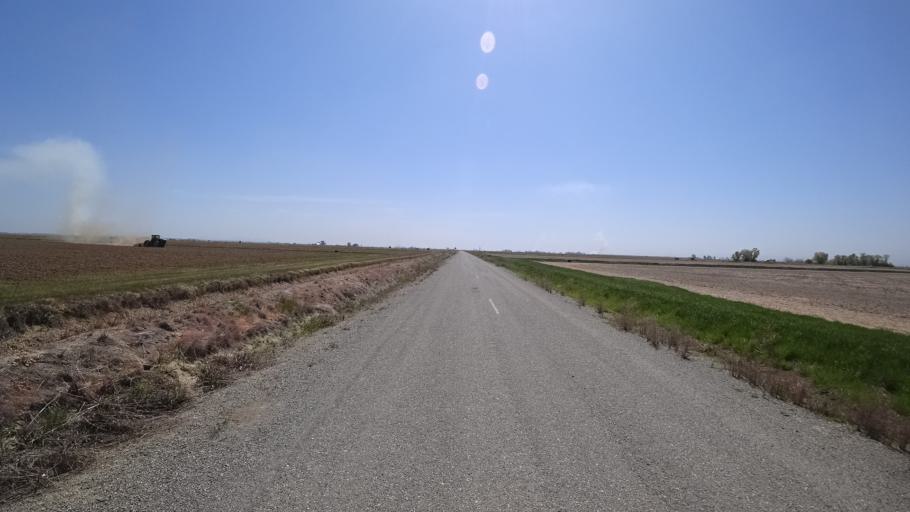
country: US
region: California
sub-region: Glenn County
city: Willows
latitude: 39.5391
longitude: -122.0887
